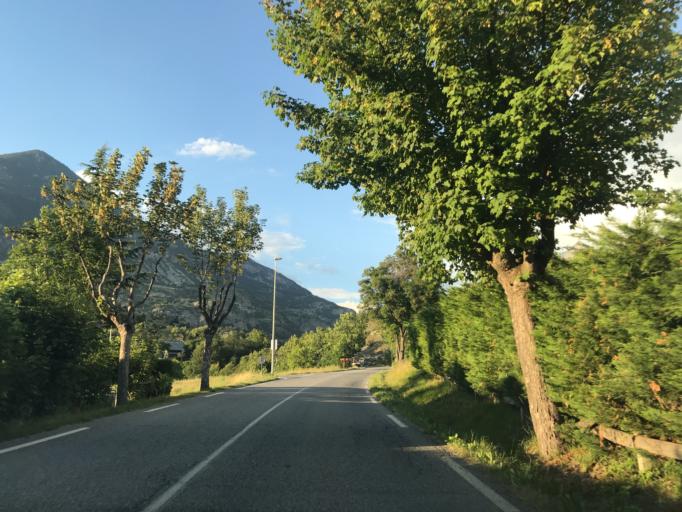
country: FR
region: Provence-Alpes-Cote d'Azur
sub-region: Departement des Hautes-Alpes
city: Guillestre
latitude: 44.6611
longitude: 6.6595
